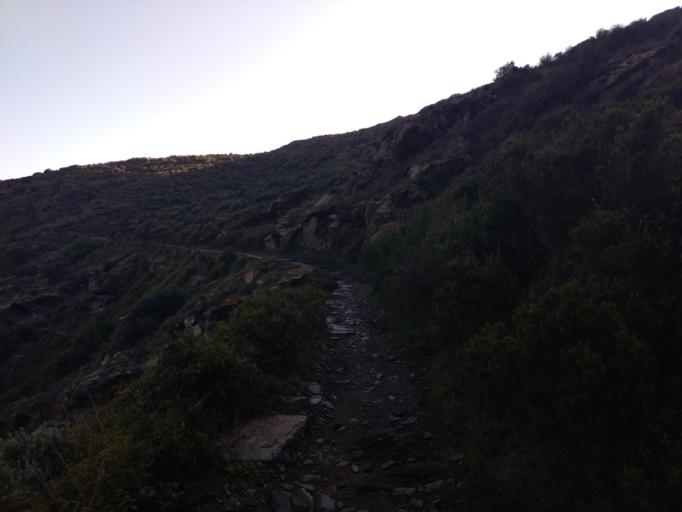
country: ES
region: Catalonia
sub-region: Provincia de Girona
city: Cadaques
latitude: 42.2693
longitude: 3.2838
